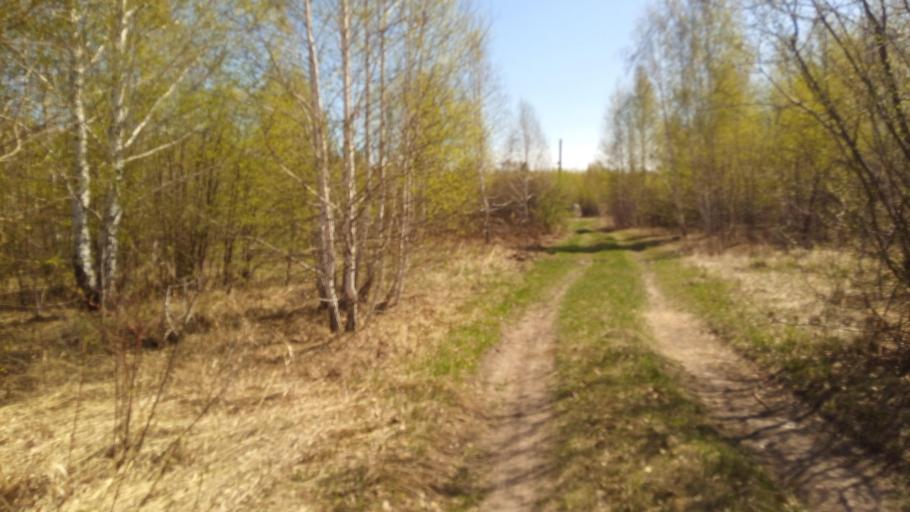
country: RU
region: Chelyabinsk
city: Timiryazevskiy
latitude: 54.9954
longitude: 60.8528
